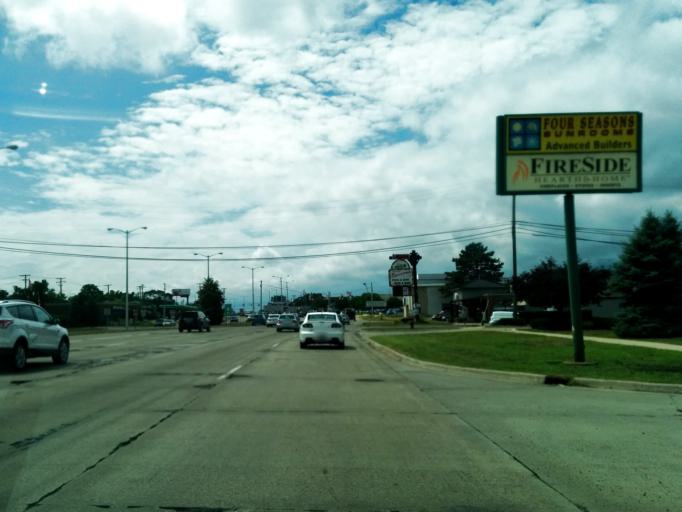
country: US
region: Michigan
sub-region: Macomb County
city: Utica
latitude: 42.6260
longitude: -83.0282
